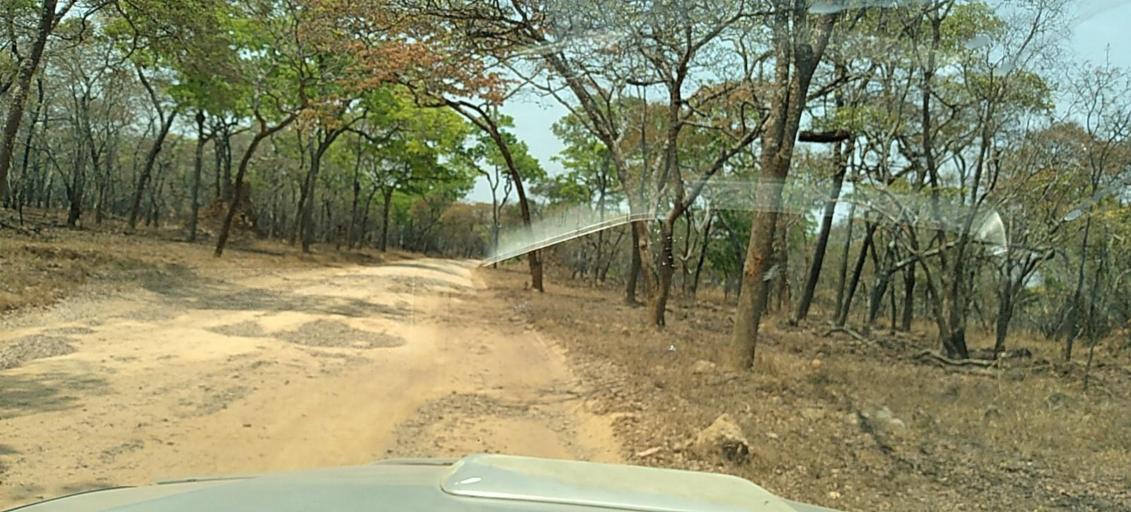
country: ZM
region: North-Western
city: Kasempa
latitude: -13.6075
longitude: 26.1821
